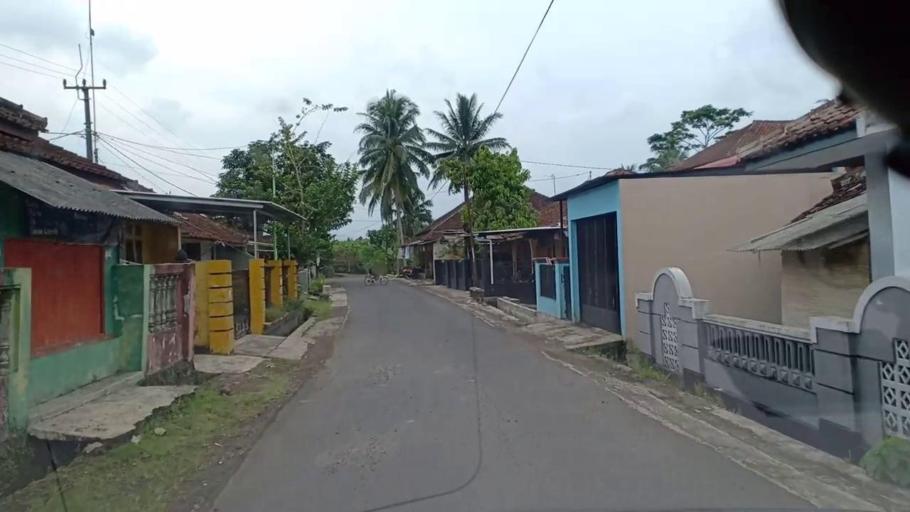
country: ID
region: West Java
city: Kertasari
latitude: -7.3392
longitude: 108.2761
